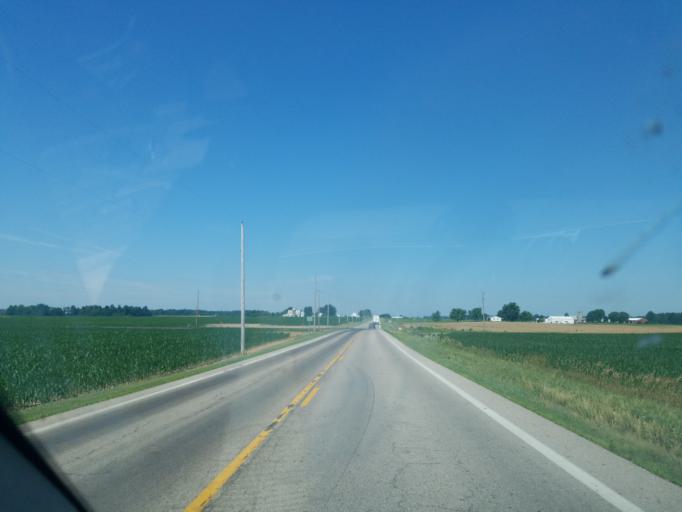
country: US
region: Ohio
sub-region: Shelby County
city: Botkins
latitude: 40.4385
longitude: -84.2197
